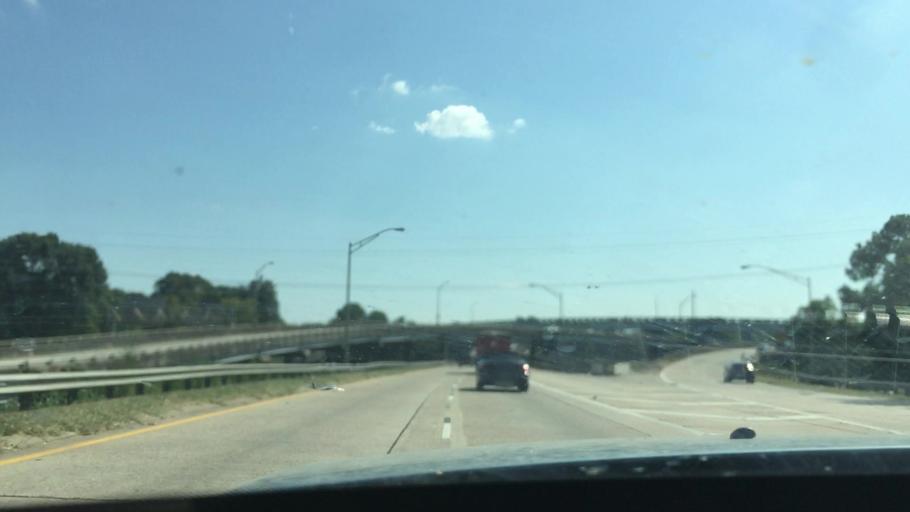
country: US
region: Louisiana
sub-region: East Baton Rouge Parish
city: Baton Rouge
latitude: 30.4420
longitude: -91.1785
